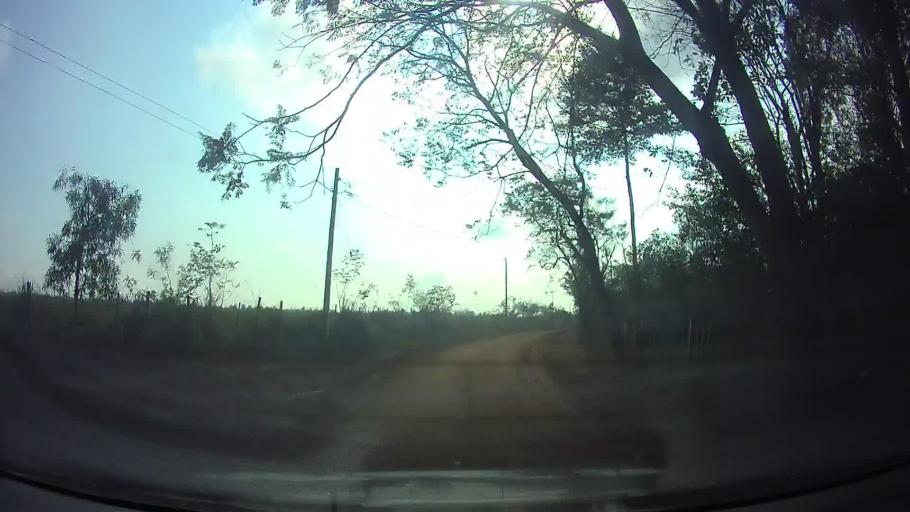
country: PY
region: Cordillera
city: Arroyos y Esteros
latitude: -25.0211
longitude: -57.1920
